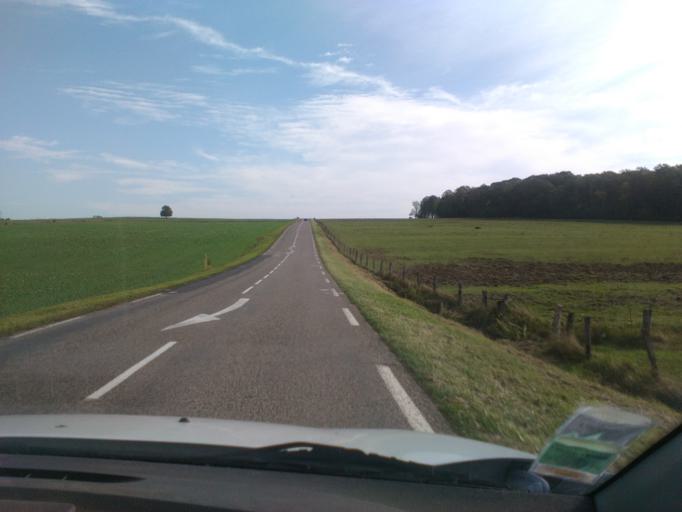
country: FR
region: Lorraine
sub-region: Departement des Vosges
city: Rambervillers
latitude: 48.3548
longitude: 6.5634
